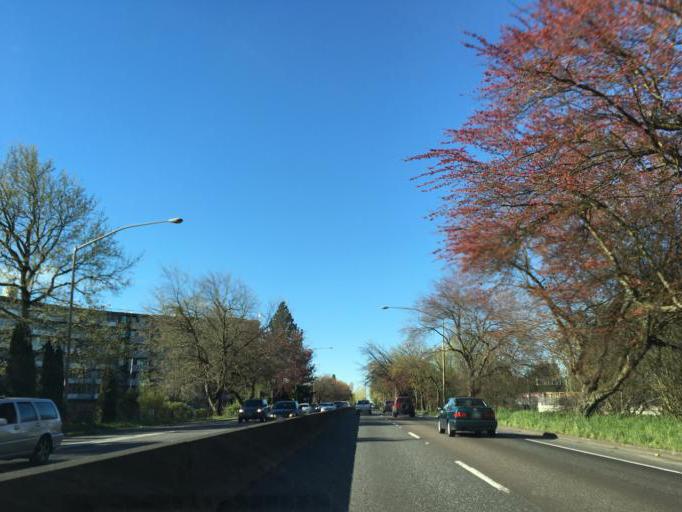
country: US
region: Oregon
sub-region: Clackamas County
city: Milwaukie
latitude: 45.4762
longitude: -122.6409
